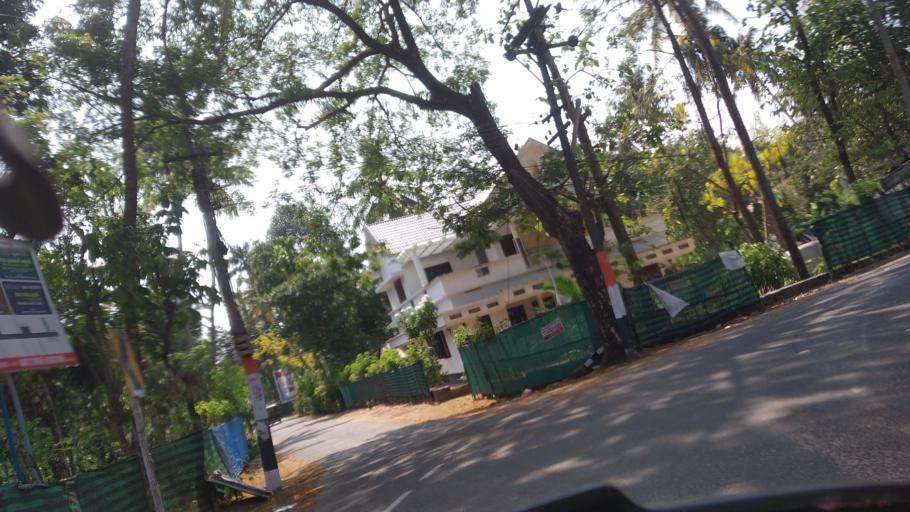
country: IN
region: Kerala
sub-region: Thrissur District
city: Thanniyam
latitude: 10.3699
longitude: 76.1056
